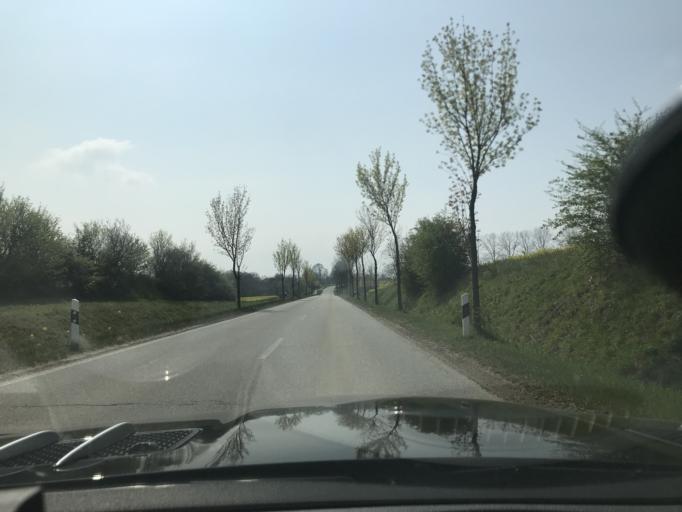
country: DE
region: Schleswig-Holstein
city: Gremersdorf
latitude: 54.3570
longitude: 10.9330
